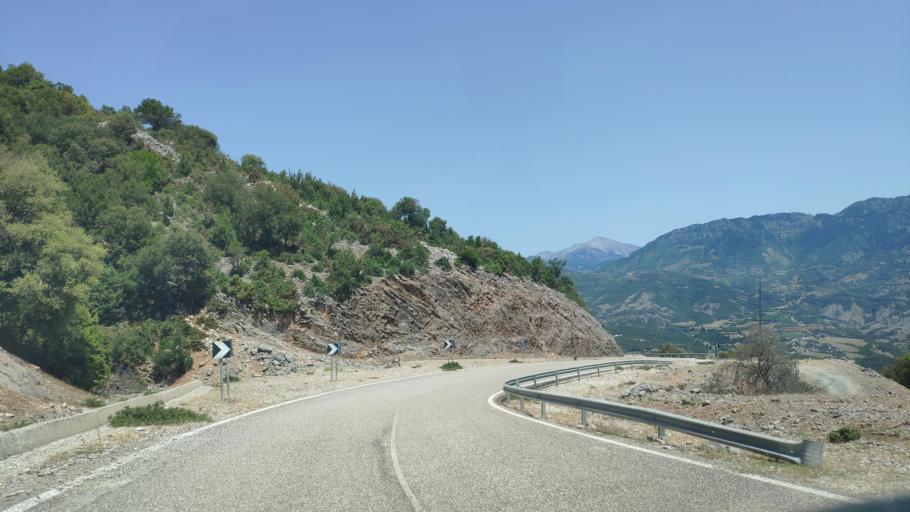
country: GR
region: Central Greece
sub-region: Nomos Evrytanias
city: Kerasochori
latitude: 39.0927
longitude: 21.4114
